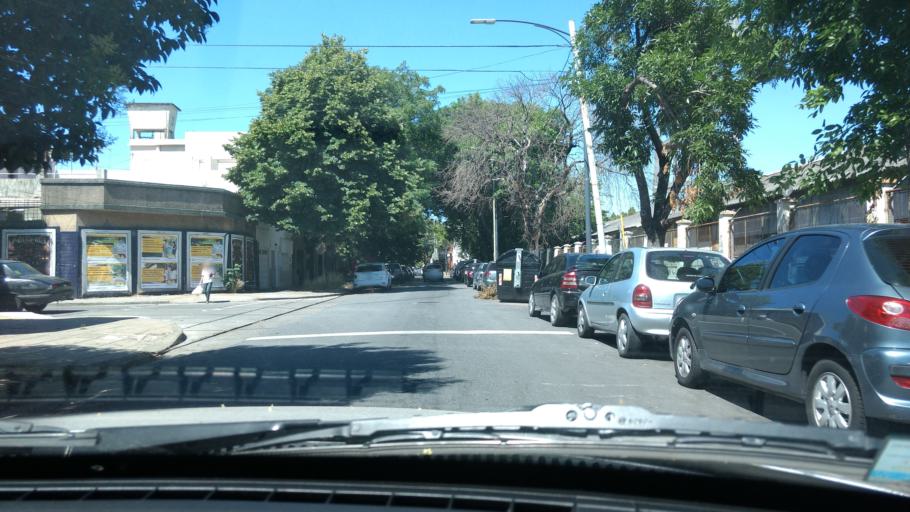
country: AR
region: Buenos Aires F.D.
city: Villa Santa Rita
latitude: -34.6219
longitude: -58.5131
